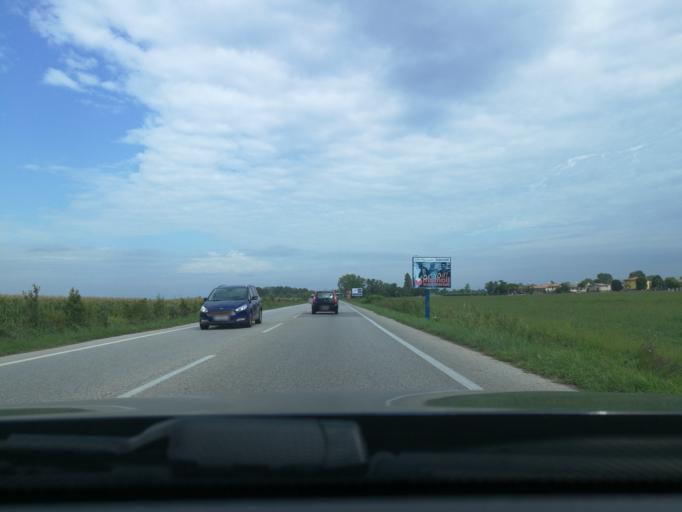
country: IT
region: Veneto
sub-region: Provincia di Venezia
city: Bibione
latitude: 45.6665
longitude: 13.0569
